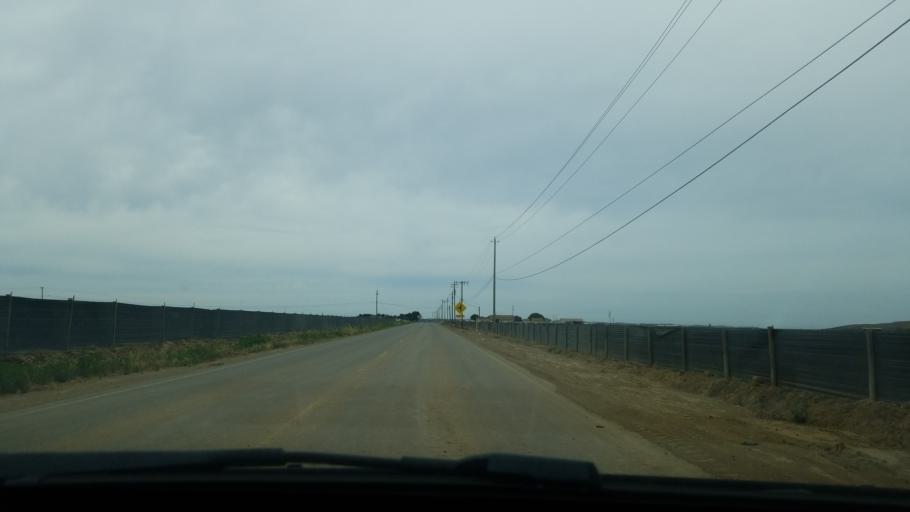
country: US
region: California
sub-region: San Luis Obispo County
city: Nipomo
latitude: 35.0041
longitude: -120.5161
